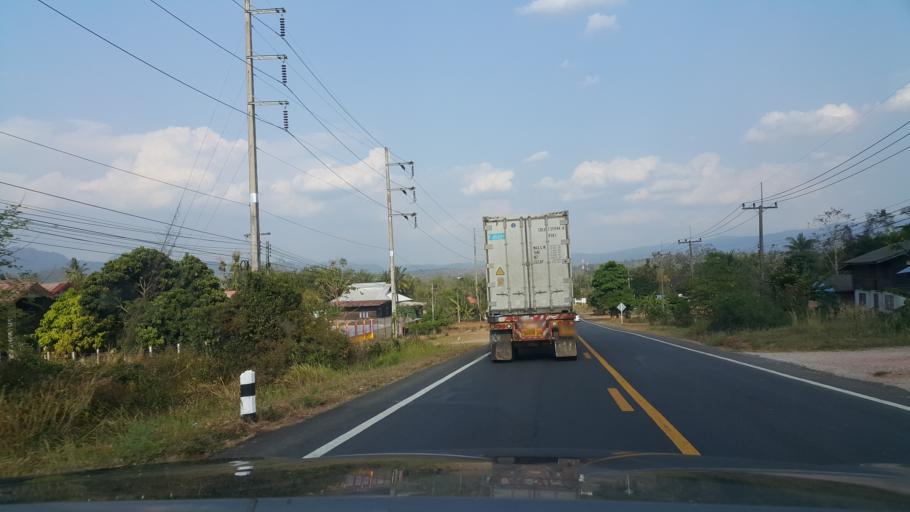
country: TH
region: Phitsanulok
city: Nakhon Thai
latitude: 17.1409
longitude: 100.9387
